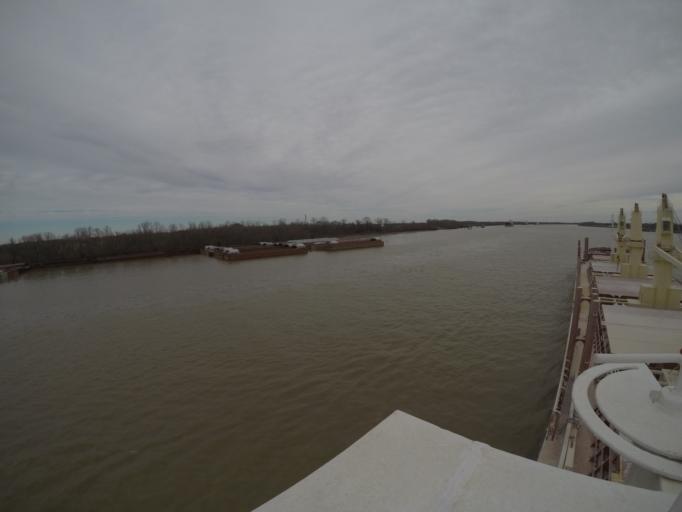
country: US
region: Louisiana
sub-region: Saint John the Baptist Parish
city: Reserve
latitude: 30.0467
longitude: -90.5309
